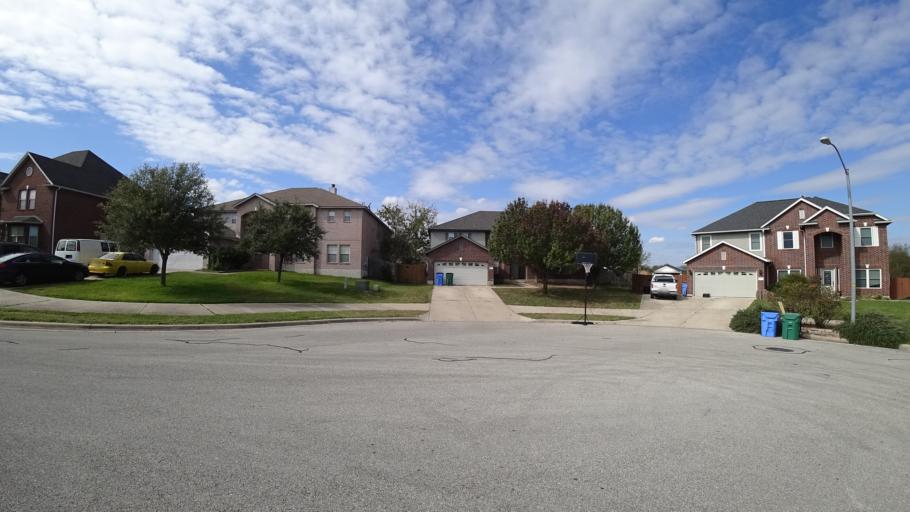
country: US
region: Texas
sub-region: Travis County
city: Pflugerville
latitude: 30.4489
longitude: -97.6264
